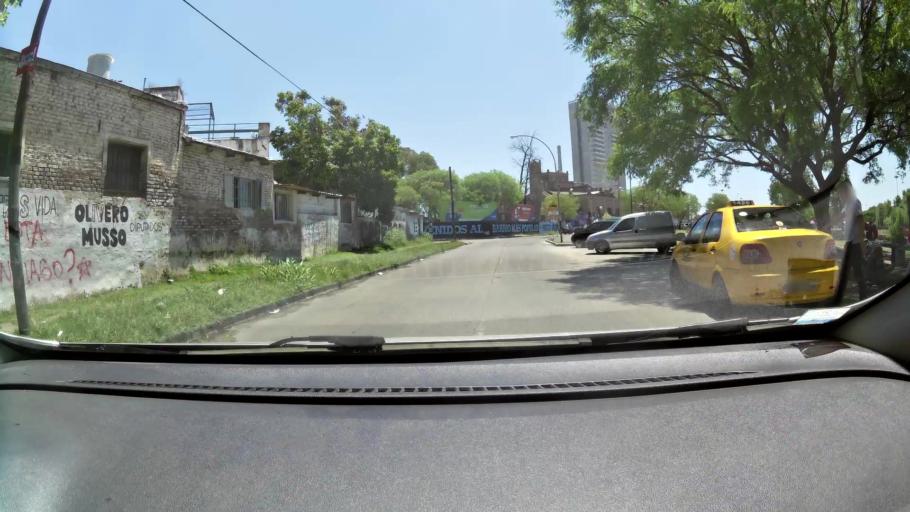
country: AR
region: Cordoba
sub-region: Departamento de Capital
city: Cordoba
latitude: -31.4035
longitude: -64.2045
